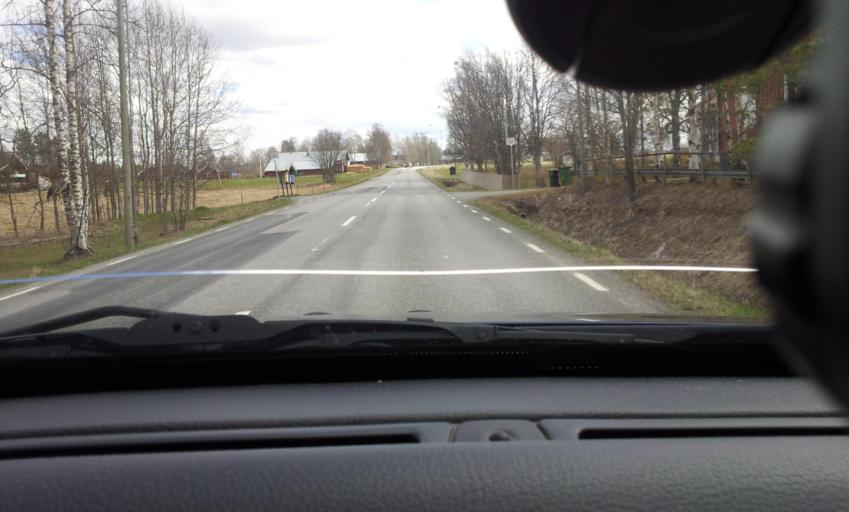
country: SE
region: Jaemtland
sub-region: OEstersunds Kommun
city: Ostersund
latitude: 63.1222
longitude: 14.7076
